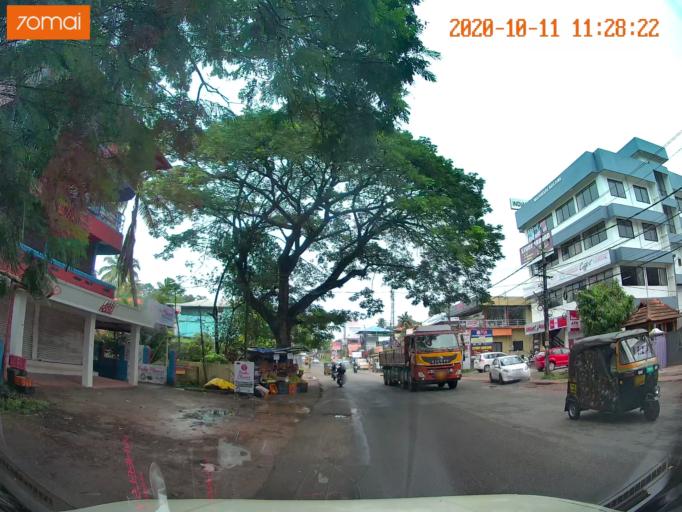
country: IN
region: Kerala
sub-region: Kottayam
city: Changanacheri
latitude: 9.4577
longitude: 76.5535
